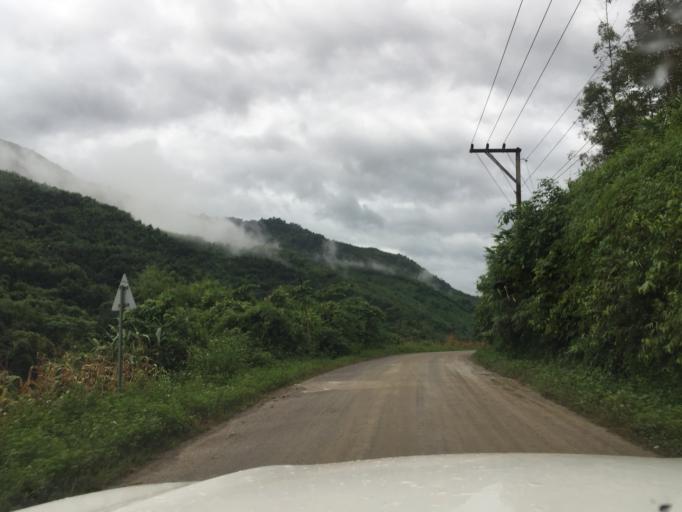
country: LA
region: Oudomxai
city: Muang La
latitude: 21.0008
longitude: 102.2329
